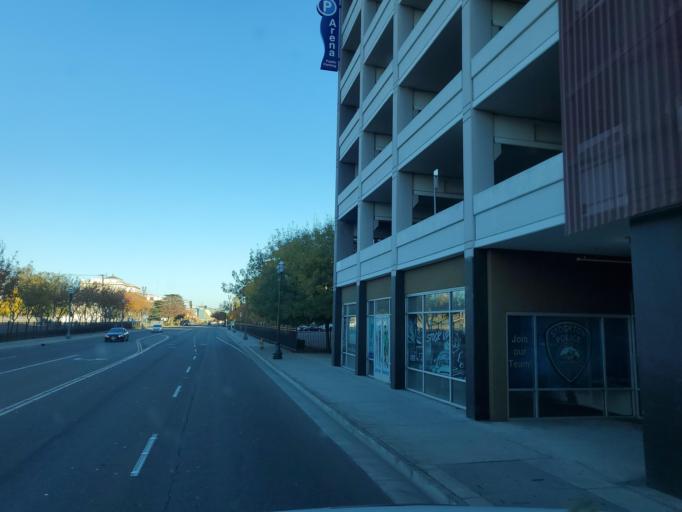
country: US
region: California
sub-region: San Joaquin County
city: Stockton
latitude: 37.9567
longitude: -121.2969
